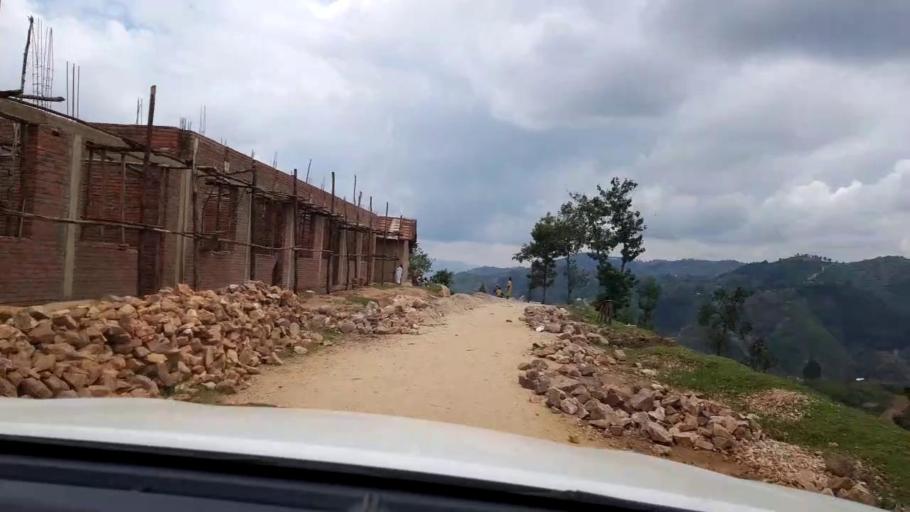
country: RW
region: Western Province
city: Kibuye
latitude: -1.8281
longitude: 29.5473
